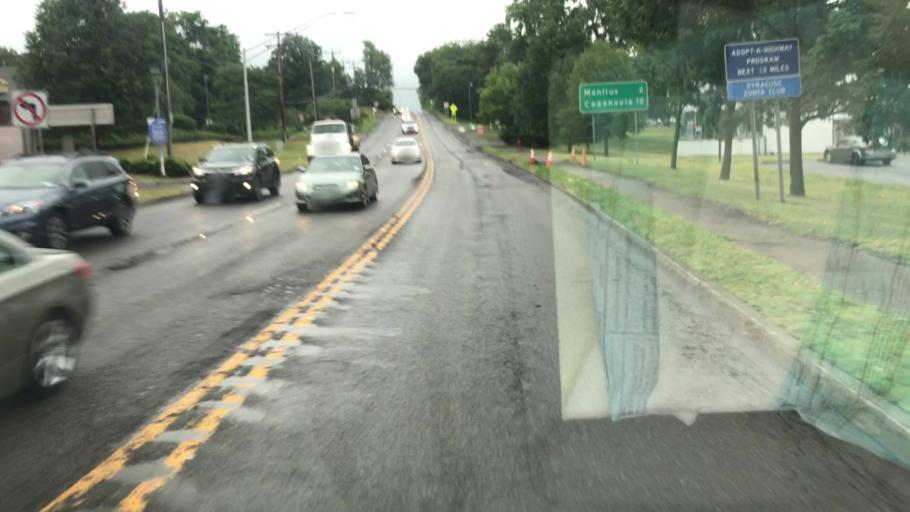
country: US
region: New York
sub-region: Onondaga County
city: Fayetteville
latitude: 43.0278
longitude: -76.0443
